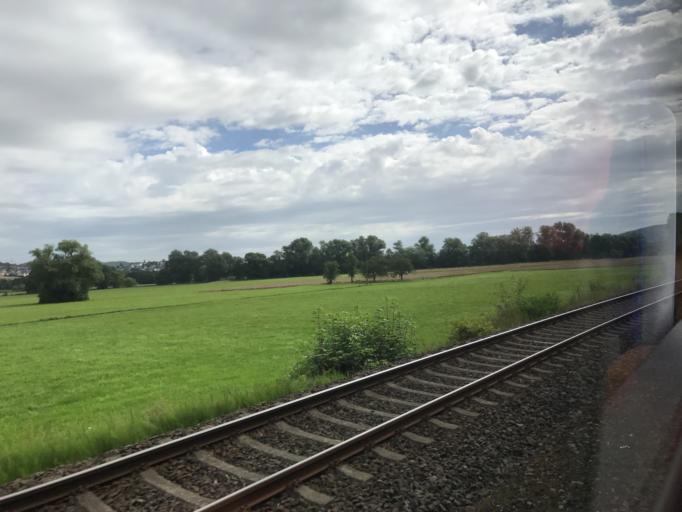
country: DE
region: Hesse
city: Burgsolms
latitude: 50.5471
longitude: 8.4021
